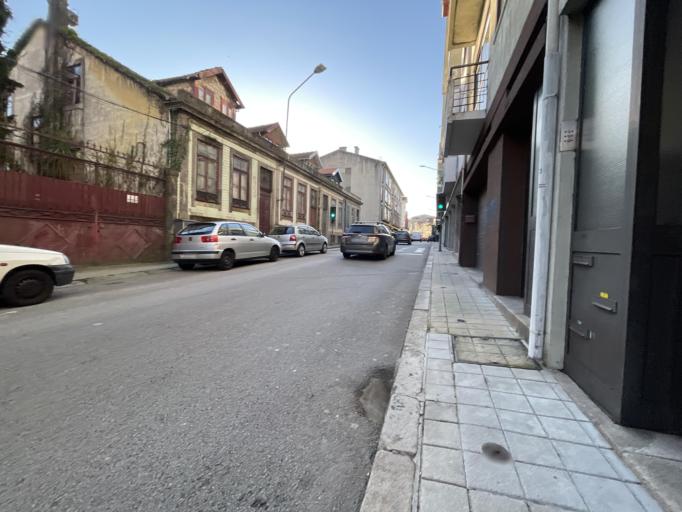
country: PT
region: Porto
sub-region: Porto
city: Porto
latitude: 41.1573
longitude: -8.5883
